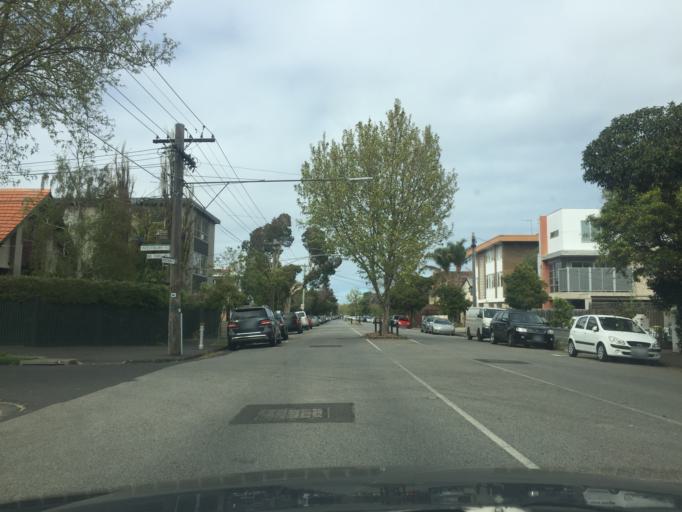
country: AU
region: Victoria
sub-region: Port Phillip
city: St Kilda East
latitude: -37.8634
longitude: 144.9965
